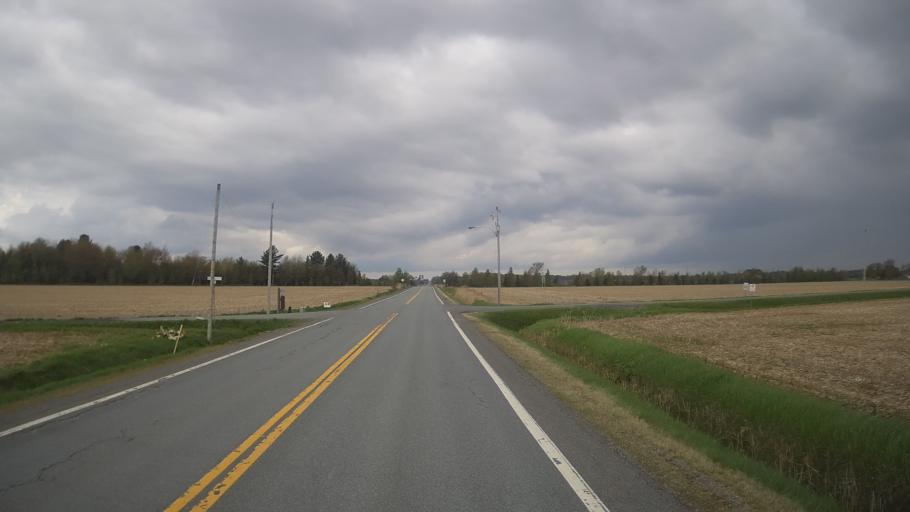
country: CA
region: Quebec
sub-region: Monteregie
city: Farnham
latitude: 45.2540
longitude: -72.9092
